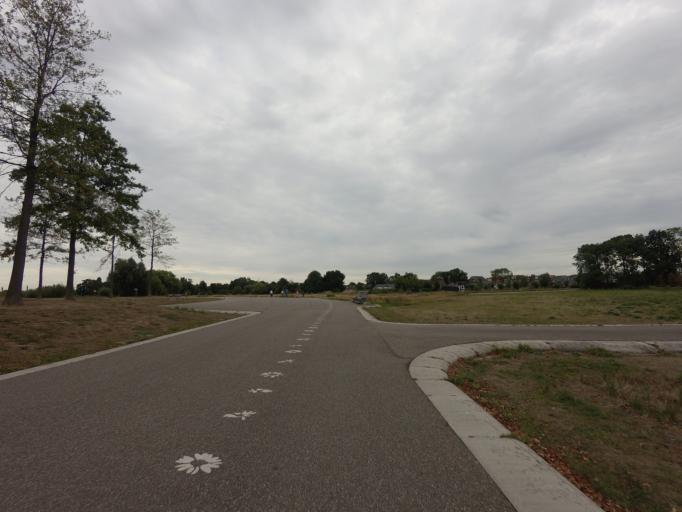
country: NL
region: Utrecht
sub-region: Stichtse Vecht
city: Spechtenkamp
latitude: 52.0955
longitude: 5.0201
